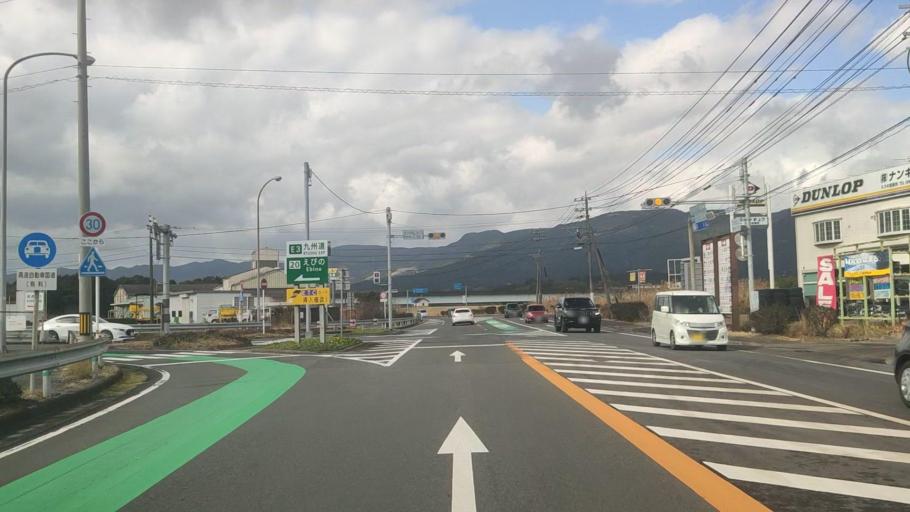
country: JP
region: Kumamoto
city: Hitoyoshi
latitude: 32.0518
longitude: 130.8047
